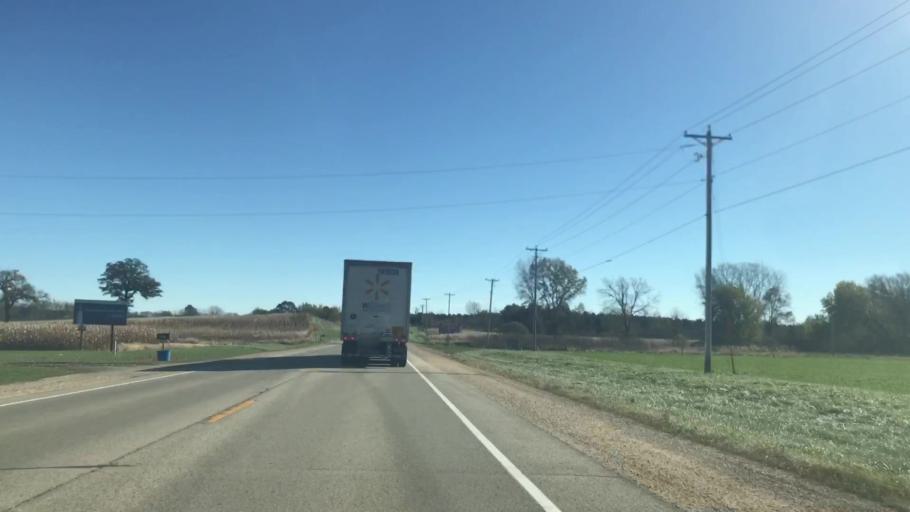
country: US
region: Wisconsin
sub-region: Dodge County
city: Juneau
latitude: 43.4448
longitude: -88.7169
